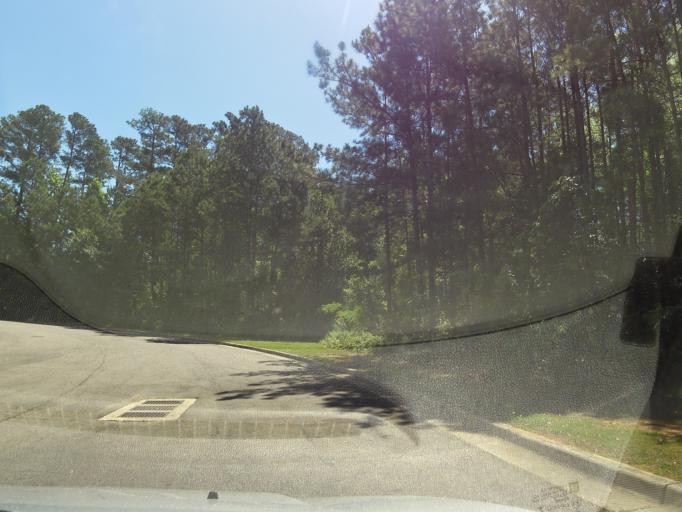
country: US
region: Georgia
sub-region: Columbia County
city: Martinez
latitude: 33.5075
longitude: -82.0310
